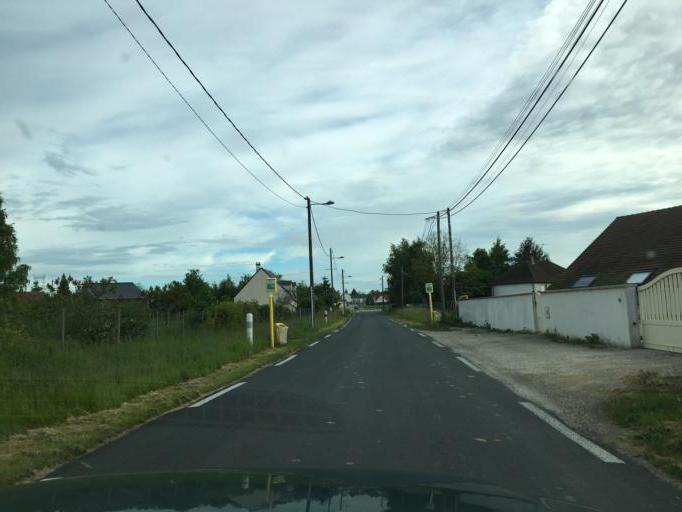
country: FR
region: Centre
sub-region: Departement du Loiret
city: Ingre
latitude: 47.9079
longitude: 1.8038
